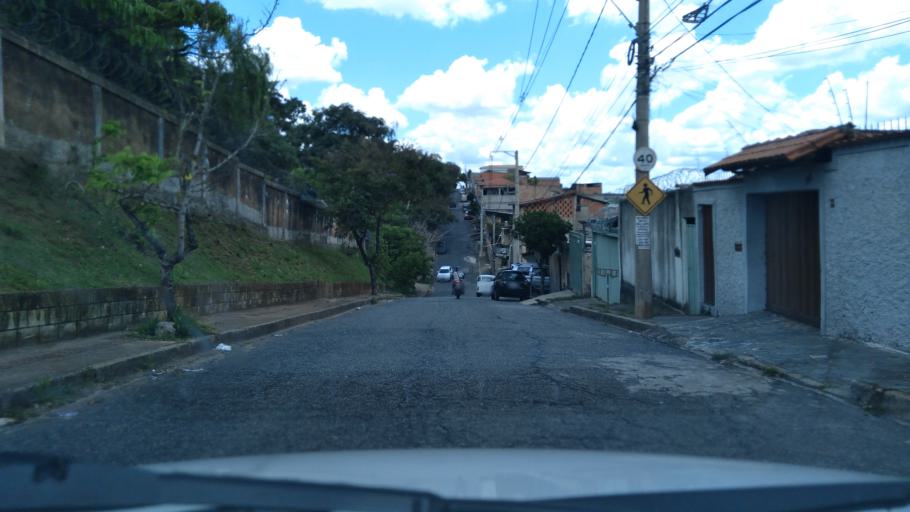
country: BR
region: Minas Gerais
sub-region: Belo Horizonte
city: Belo Horizonte
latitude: -19.9160
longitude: -43.8949
